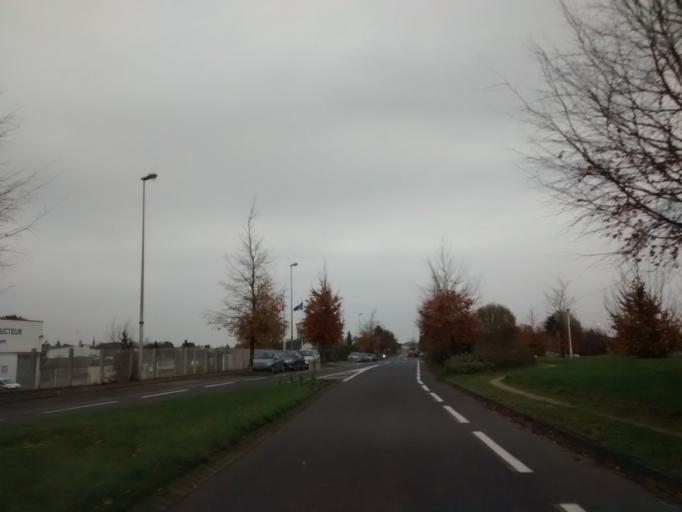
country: FR
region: Brittany
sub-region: Departement d'Ille-et-Vilaine
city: Noyal-sur-Vilaine
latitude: 48.1106
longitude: -1.5325
